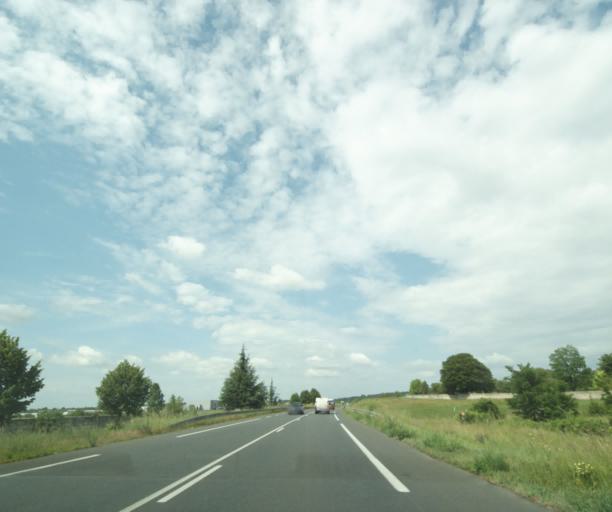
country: FR
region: Pays de la Loire
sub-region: Departement de Maine-et-Loire
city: Distre
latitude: 47.2234
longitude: -0.1169
